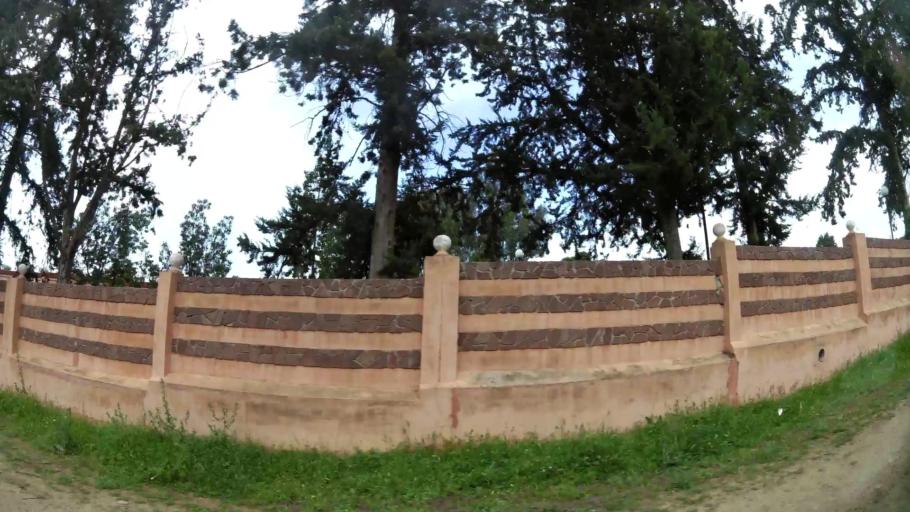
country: MA
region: Rabat-Sale-Zemmour-Zaer
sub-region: Khemisset
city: Khemisset
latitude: 33.7446
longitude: -6.1985
